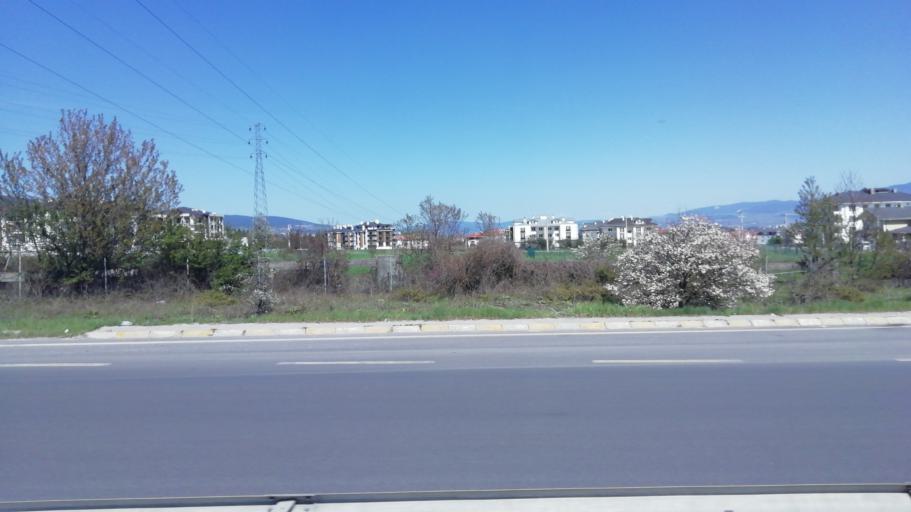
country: TR
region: Bolu
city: Bolu
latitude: 40.7395
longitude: 31.5648
